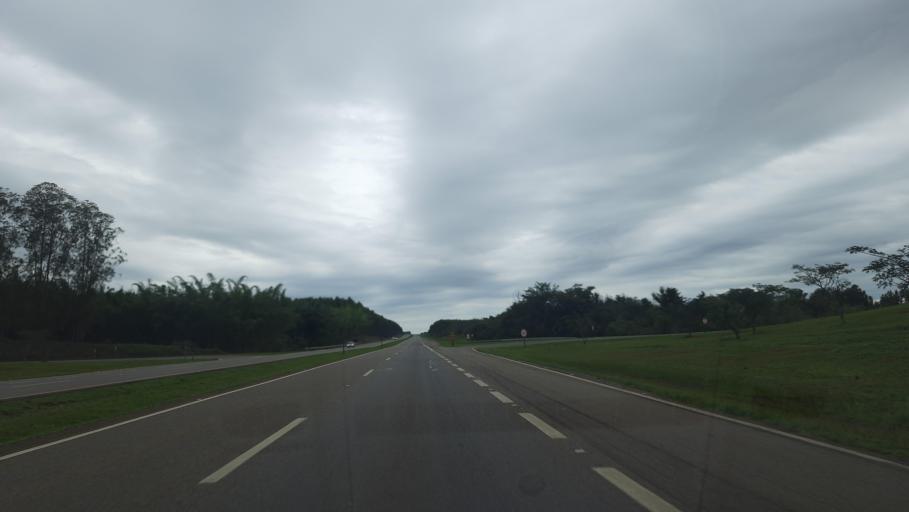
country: BR
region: Sao Paulo
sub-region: Casa Branca
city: Casa Branca
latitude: -21.8574
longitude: -47.0631
